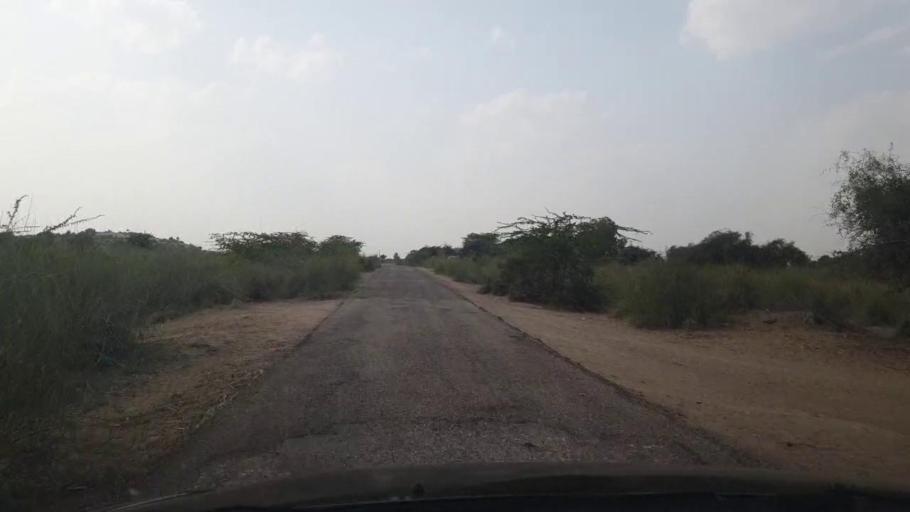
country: PK
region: Sindh
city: Islamkot
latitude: 24.9887
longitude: 70.5723
